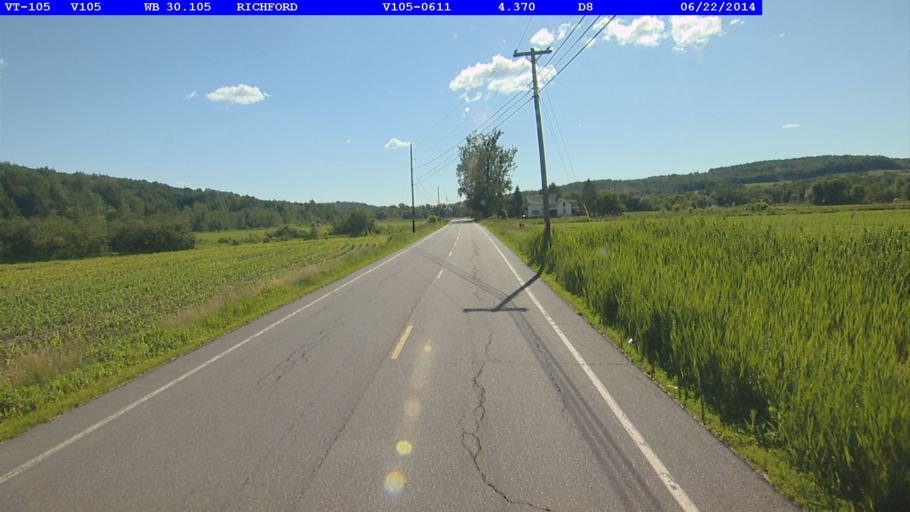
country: US
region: Vermont
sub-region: Franklin County
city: Richford
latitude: 44.9944
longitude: -72.6336
